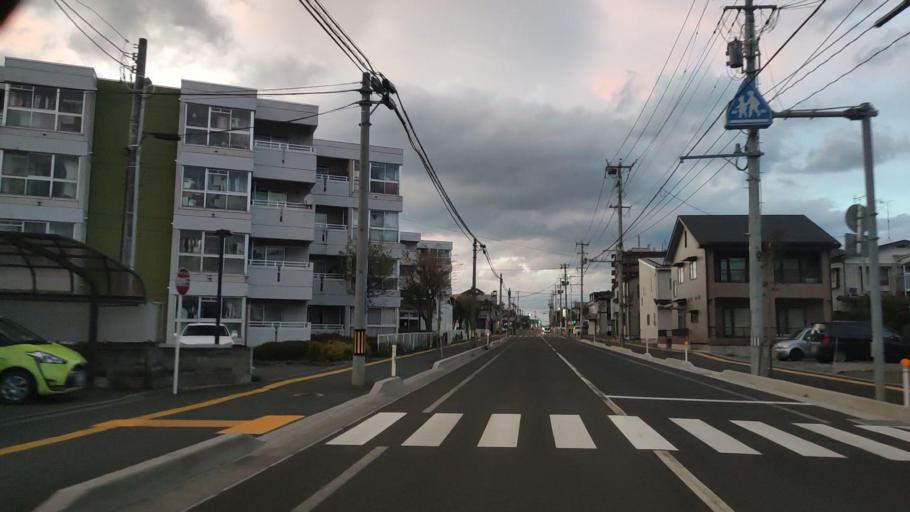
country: JP
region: Iwate
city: Morioka-shi
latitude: 39.7200
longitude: 141.1086
